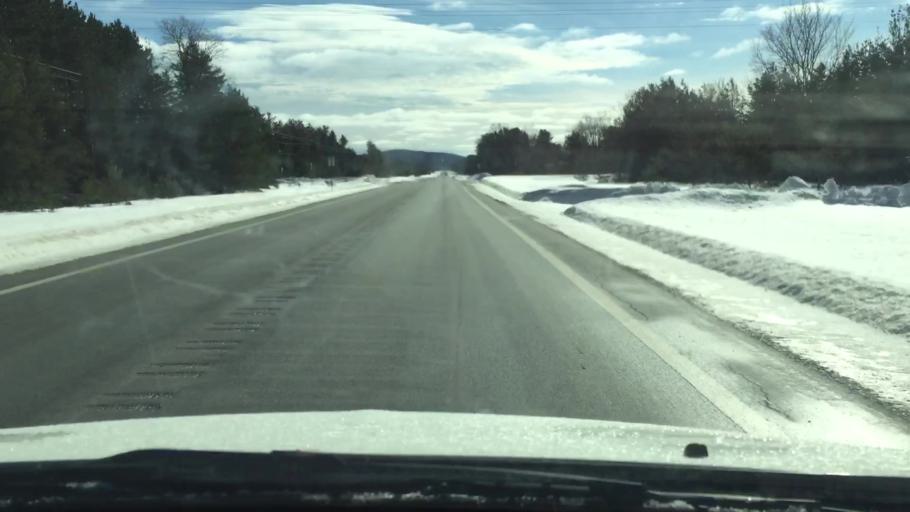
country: US
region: Michigan
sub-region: Antrim County
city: Mancelona
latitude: 44.9325
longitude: -85.0509
